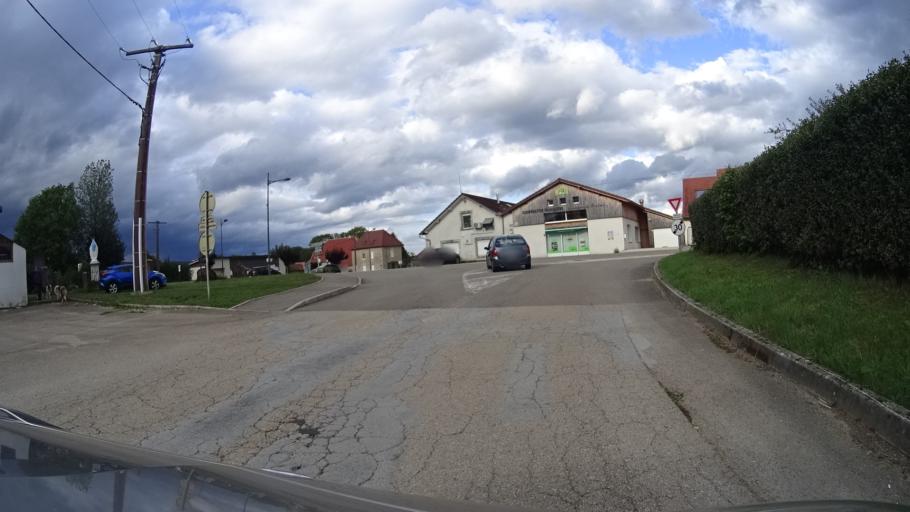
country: FR
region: Franche-Comte
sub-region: Departement du Doubs
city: Nancray
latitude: 47.2437
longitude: 6.1767
